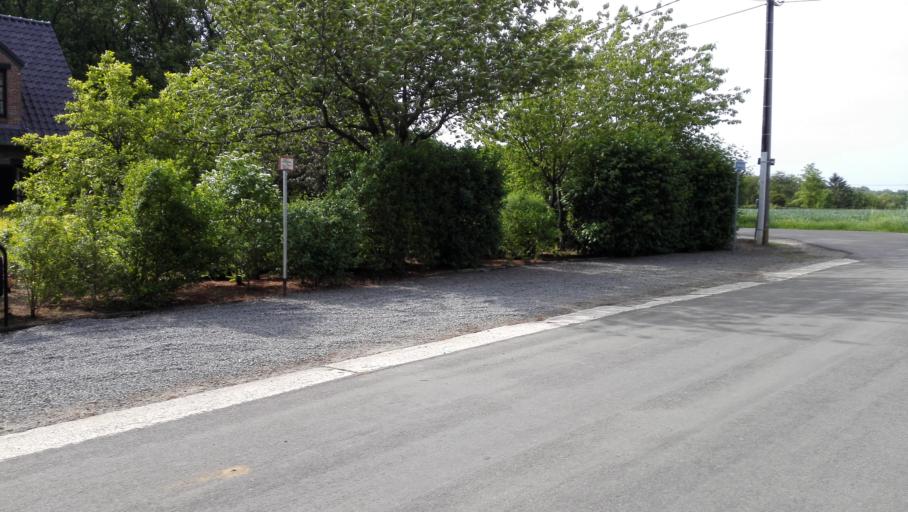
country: BE
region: Flanders
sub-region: Provincie Vlaams-Brabant
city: Holsbeek
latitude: 50.9075
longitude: 4.7799
